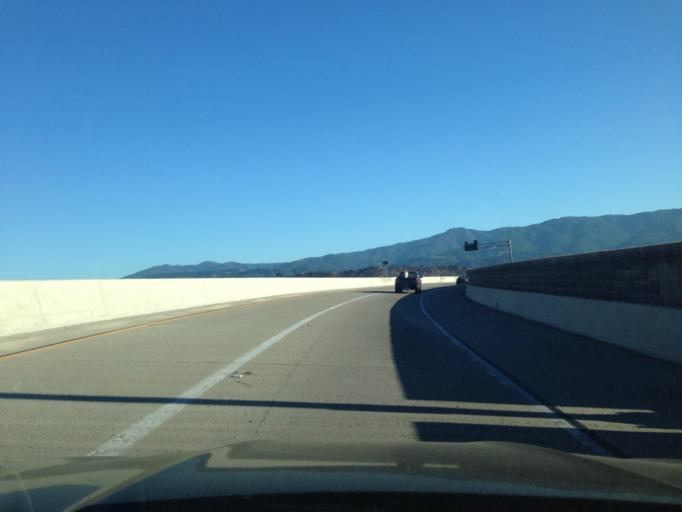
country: US
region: California
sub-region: Santa Clara County
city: Seven Trees
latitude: 37.2583
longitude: -121.8593
